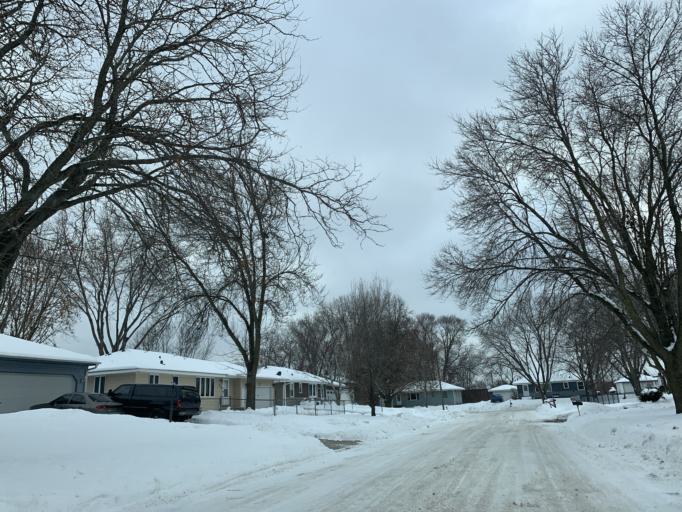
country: US
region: Minnesota
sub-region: Anoka County
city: Coon Rapids
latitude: 45.1662
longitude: -93.2857
